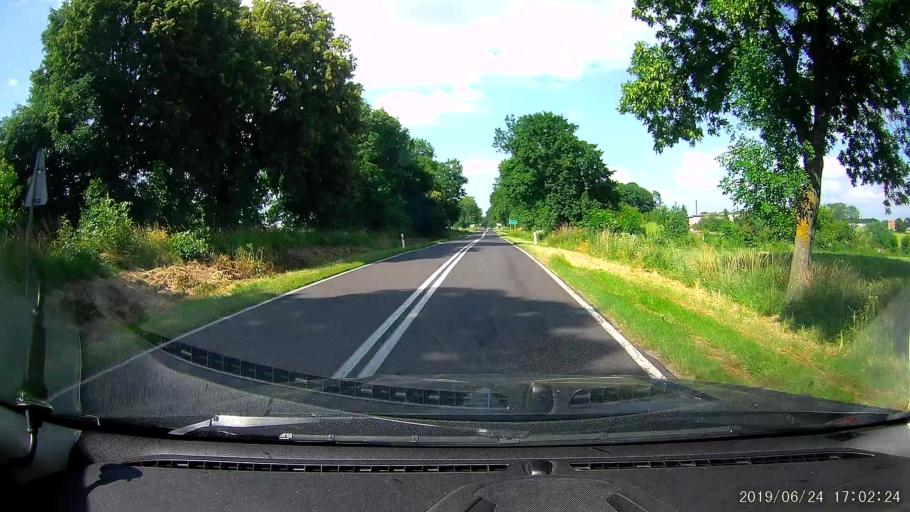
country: PL
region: Lublin Voivodeship
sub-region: Powiat tomaszowski
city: Telatyn
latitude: 50.5513
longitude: 23.9322
